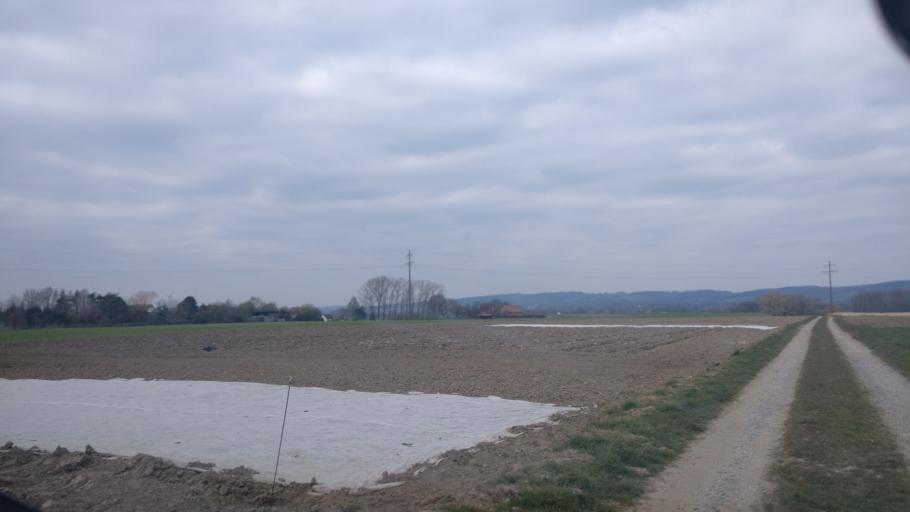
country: DE
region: North Rhine-Westphalia
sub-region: Regierungsbezirk Detmold
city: Lage
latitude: 52.0192
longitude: 8.7875
